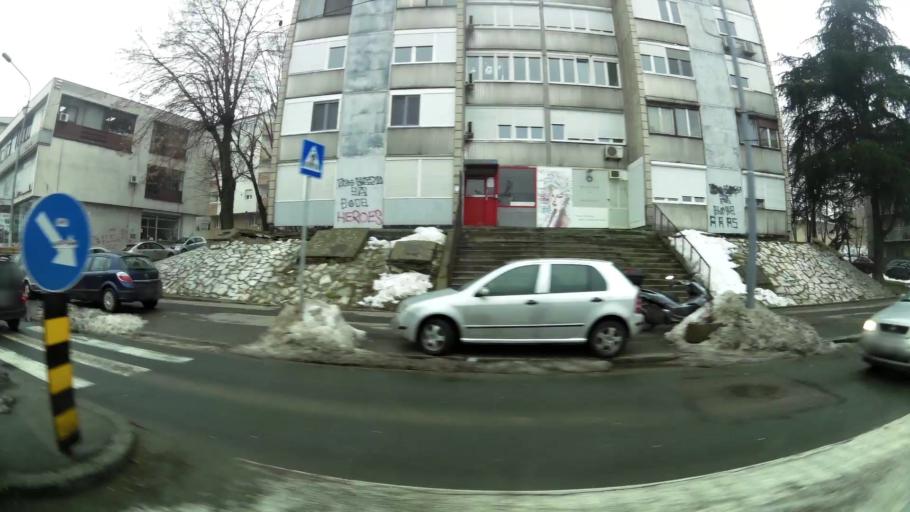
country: RS
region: Central Serbia
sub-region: Belgrade
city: Vracar
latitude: 44.7861
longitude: 20.4723
